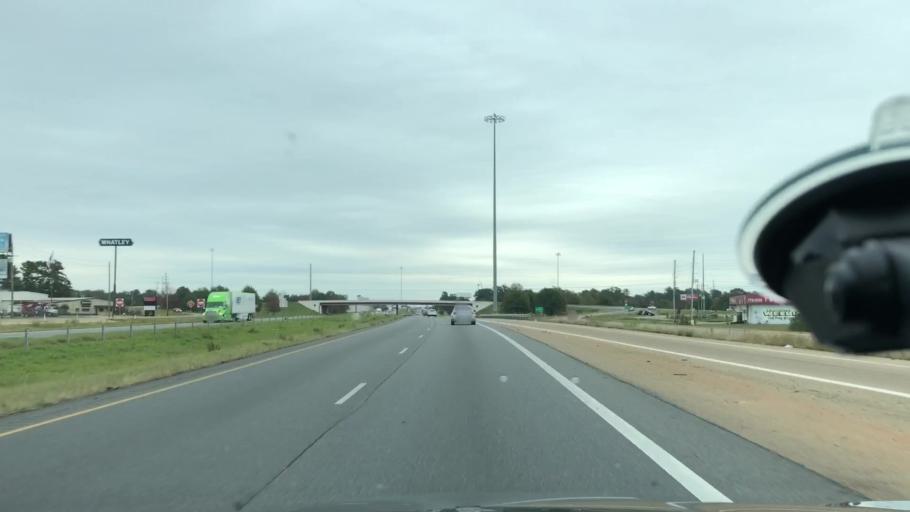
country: US
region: Arkansas
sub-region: Miller County
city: Texarkana
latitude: 33.4703
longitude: -94.0334
